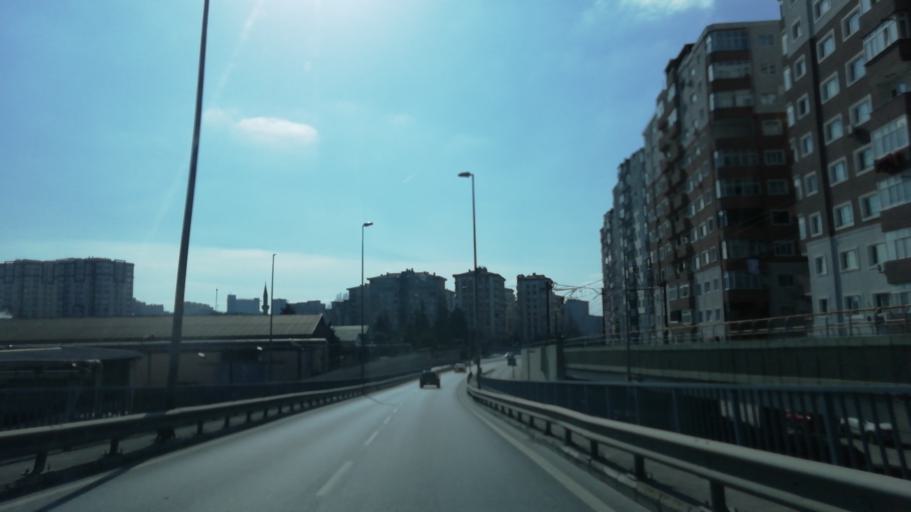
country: TR
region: Istanbul
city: merter keresteciler
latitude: 41.0195
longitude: 28.9008
